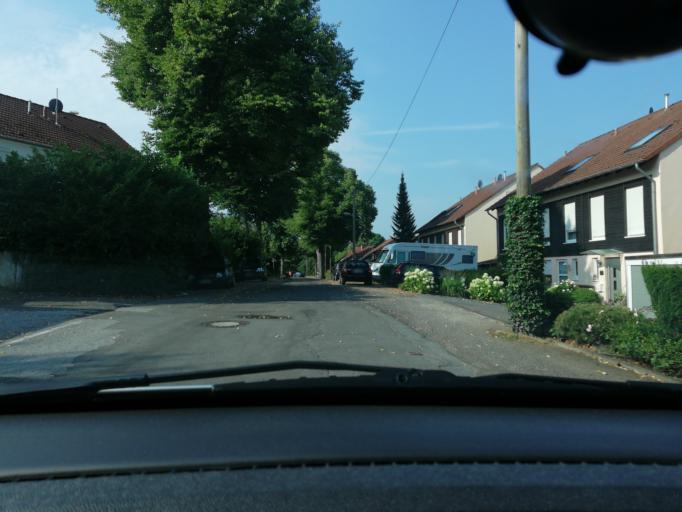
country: DE
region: North Rhine-Westphalia
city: Wetter (Ruhr)
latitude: 51.3634
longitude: 7.3654
